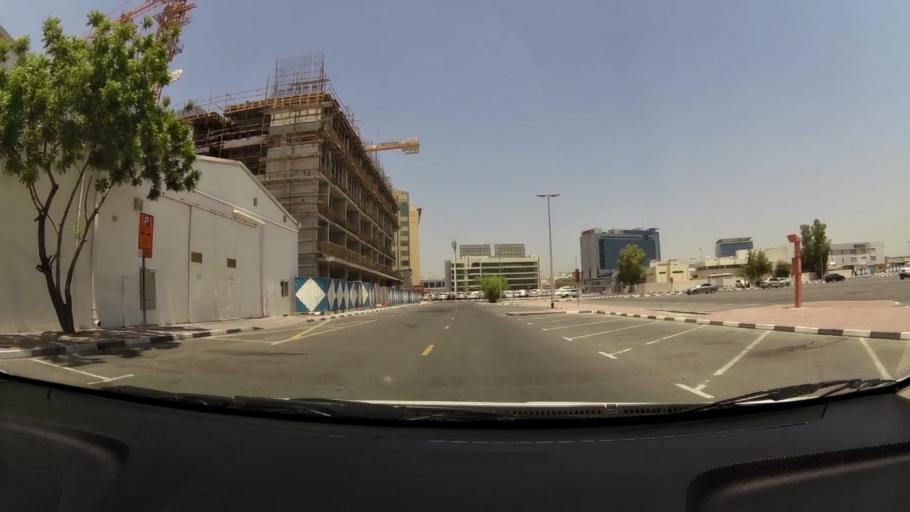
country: AE
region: Ash Shariqah
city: Sharjah
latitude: 25.2576
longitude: 55.3354
